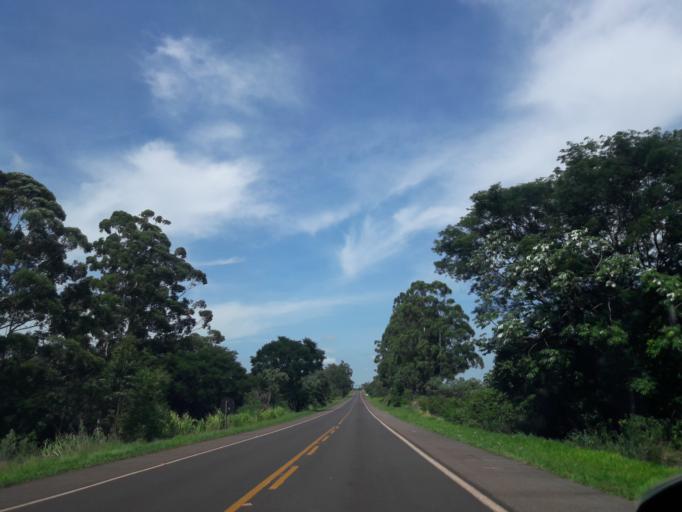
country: BR
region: Parana
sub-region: Campo Mourao
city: Campo Mourao
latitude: -24.2786
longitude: -52.5282
